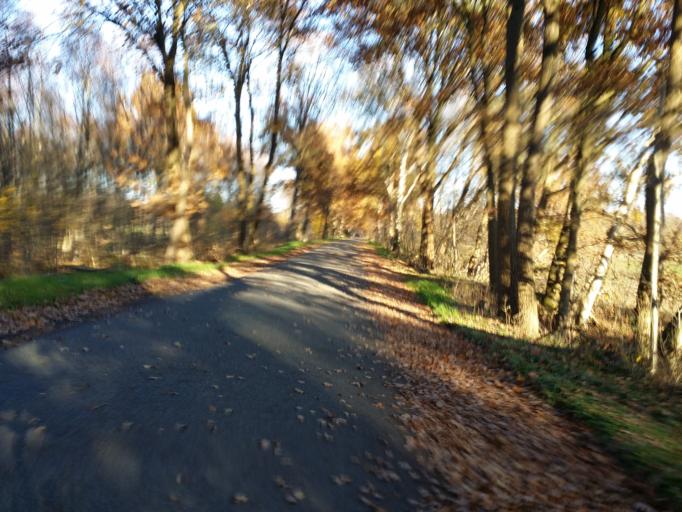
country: DE
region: Lower Saxony
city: Langwedel
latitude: 53.0260
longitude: 9.1788
